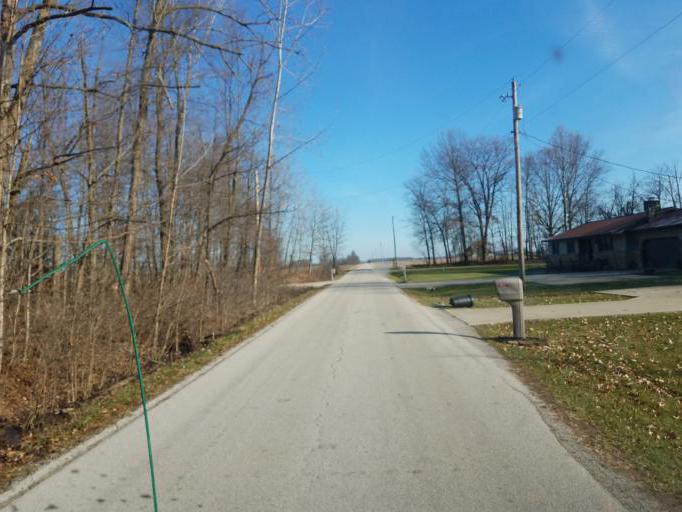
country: US
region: Ohio
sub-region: Morrow County
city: Cardington
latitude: 40.6016
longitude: -82.9269
